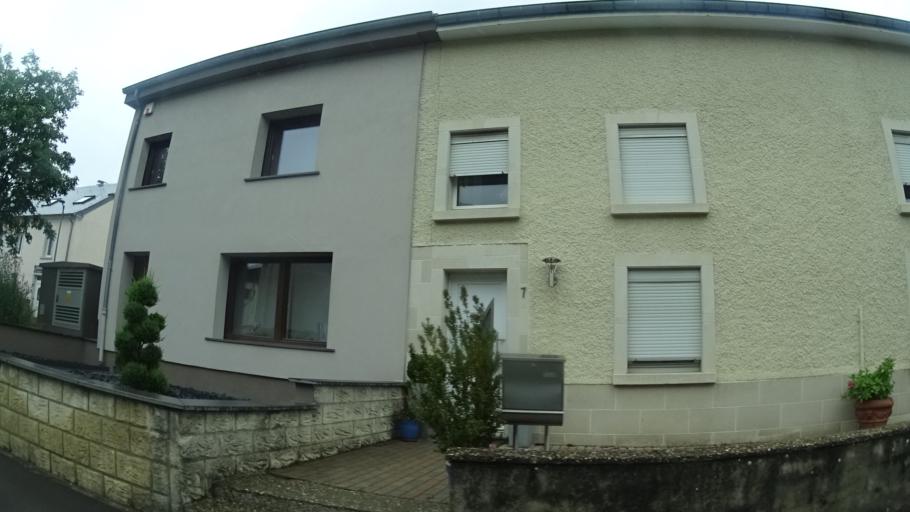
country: LU
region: Luxembourg
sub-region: Canton de Capellen
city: Bascharage
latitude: 49.5669
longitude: 5.9130
